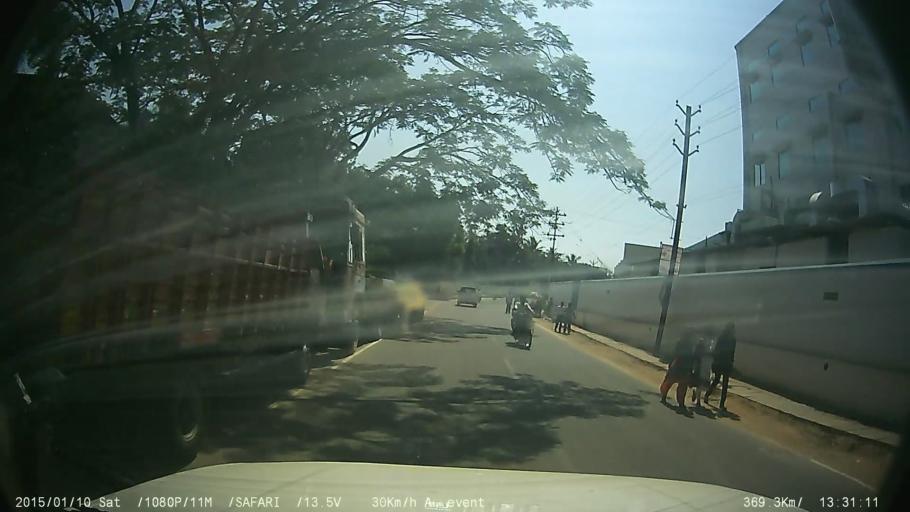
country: IN
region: Tamil Nadu
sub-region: Krishnagiri
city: Hosur
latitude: 12.7649
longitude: 77.7960
